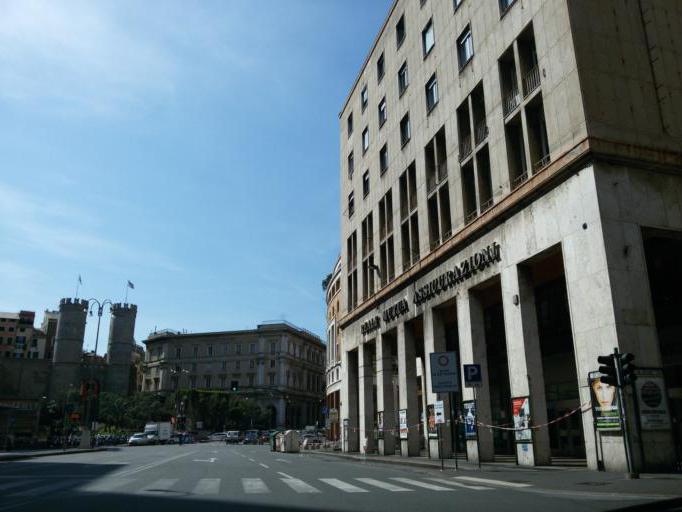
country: IT
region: Liguria
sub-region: Provincia di Genova
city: San Teodoro
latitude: 44.4050
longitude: 8.9366
